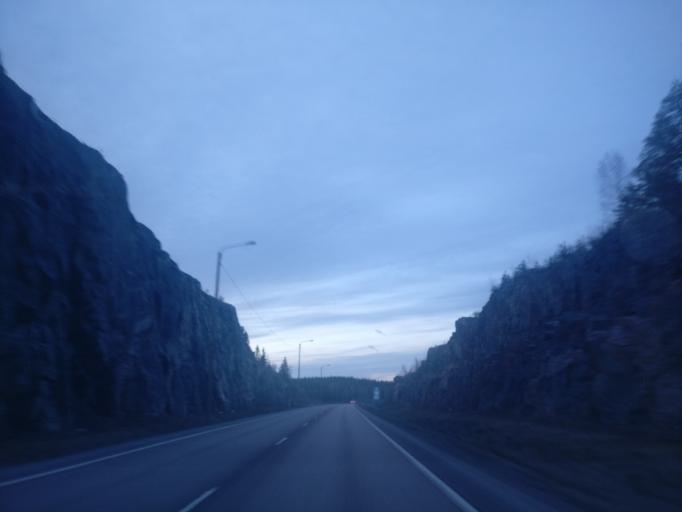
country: FI
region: Central Finland
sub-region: Jyvaeskylae
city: Saeynaetsalo
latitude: 62.2066
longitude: 25.8899
